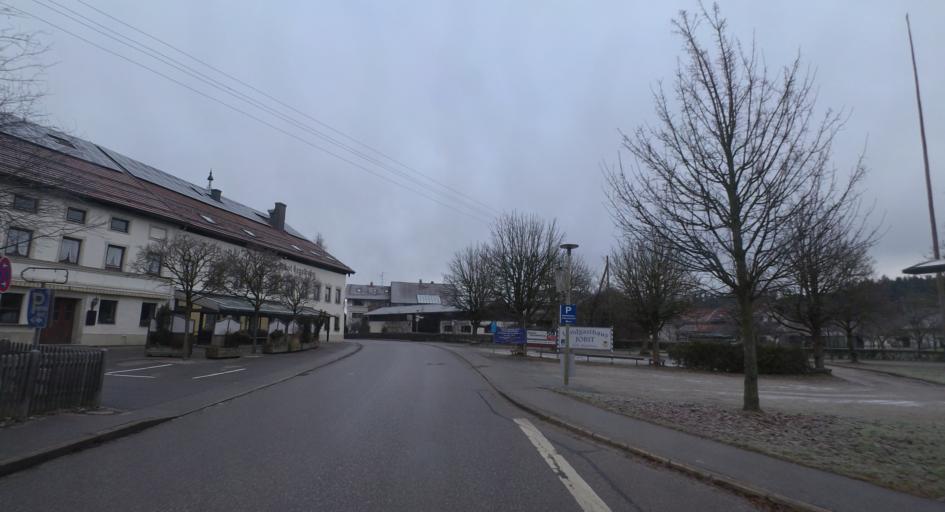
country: DE
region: Bavaria
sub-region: Upper Bavaria
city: Traunstein
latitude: 47.9127
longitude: 12.6501
